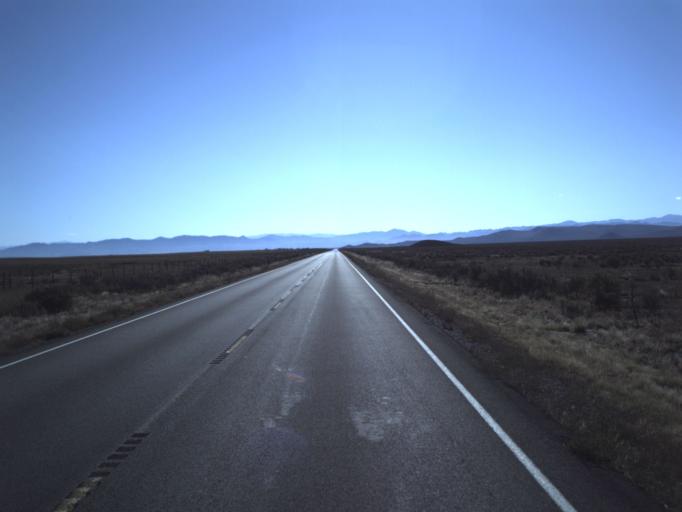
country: US
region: Utah
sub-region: Washington County
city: Enterprise
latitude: 37.7820
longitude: -113.8629
